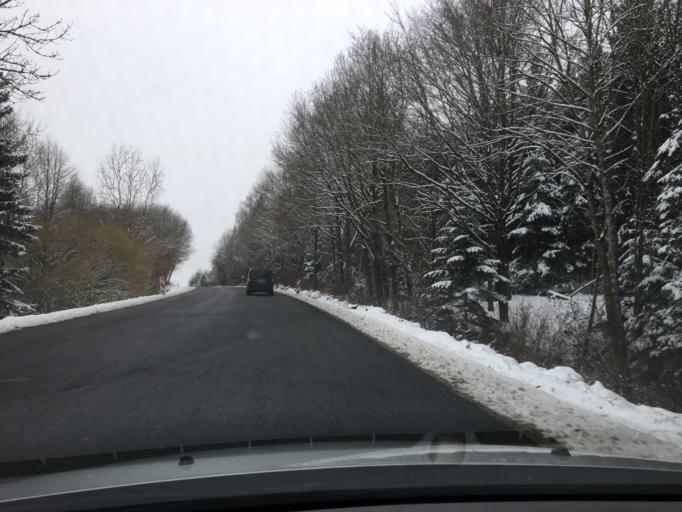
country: DE
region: Bavaria
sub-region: Upper Bavaria
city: Egglkofen
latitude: 48.4137
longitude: 12.4322
